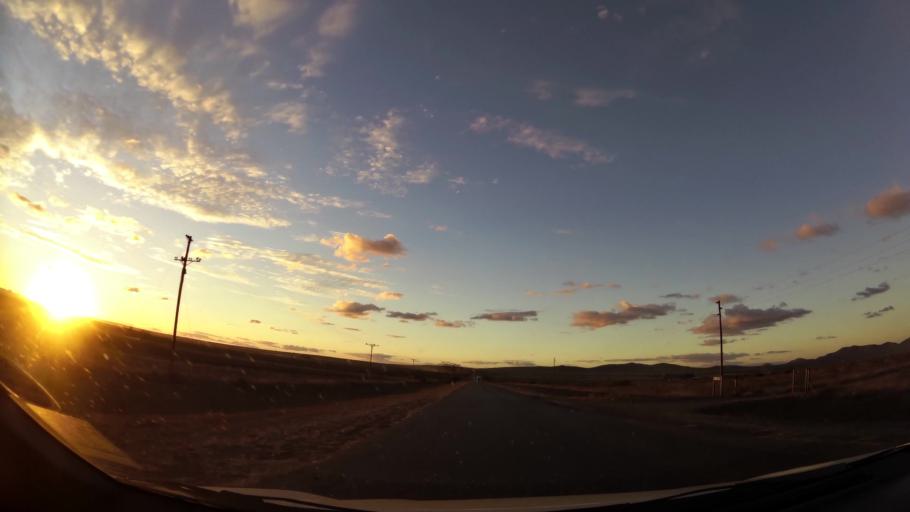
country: ZA
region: Limpopo
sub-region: Capricorn District Municipality
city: Polokwane
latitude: -23.7588
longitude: 29.4735
